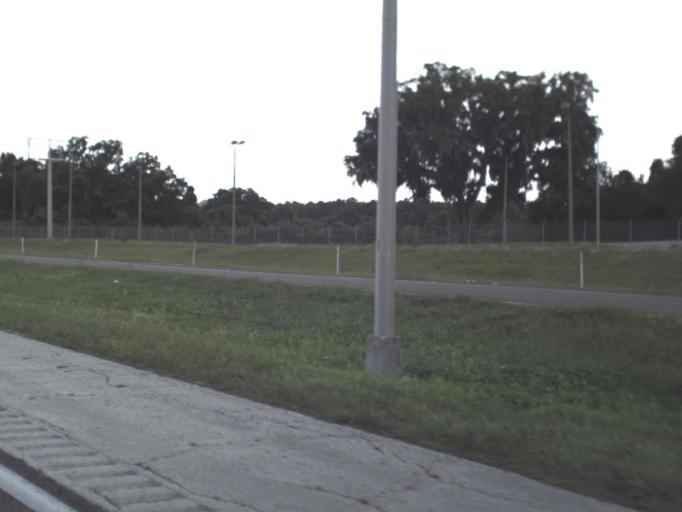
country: US
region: Florida
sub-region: Alachua County
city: Alachua
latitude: 29.6864
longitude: -82.4443
